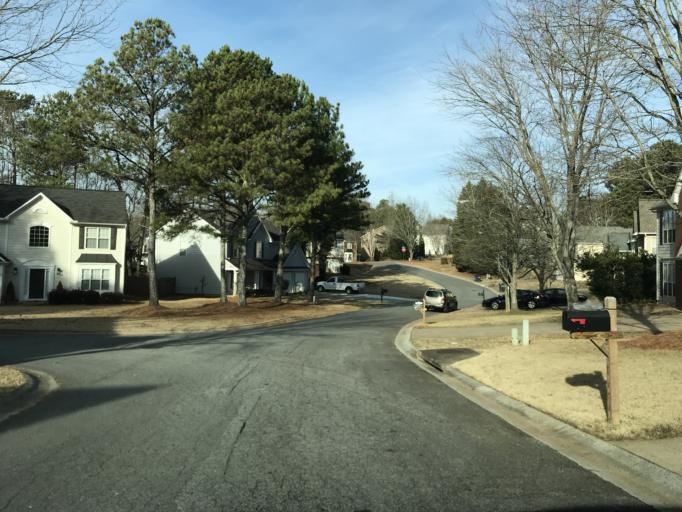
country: US
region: Georgia
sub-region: Cobb County
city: Kennesaw
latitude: 34.0584
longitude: -84.5952
